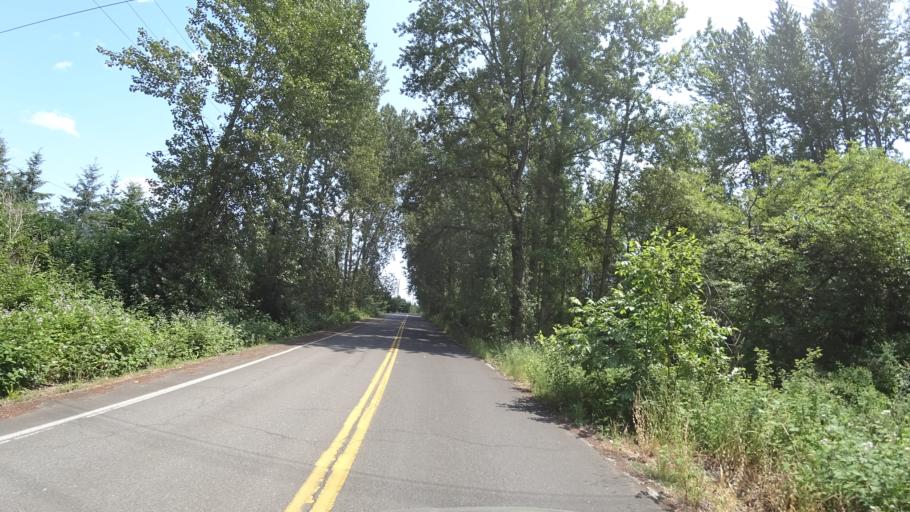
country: US
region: Washington
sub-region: Clark County
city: Lake Shore
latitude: 45.6422
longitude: -122.7655
